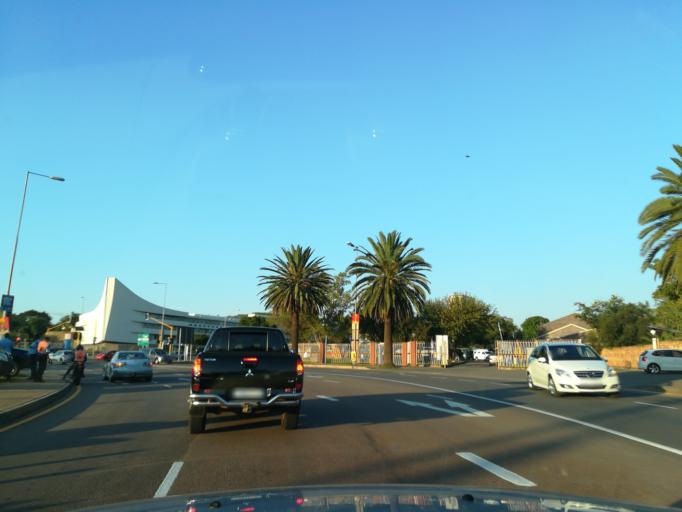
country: ZA
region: Gauteng
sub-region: City of Tshwane Metropolitan Municipality
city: Pretoria
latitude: -25.7566
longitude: 28.2247
